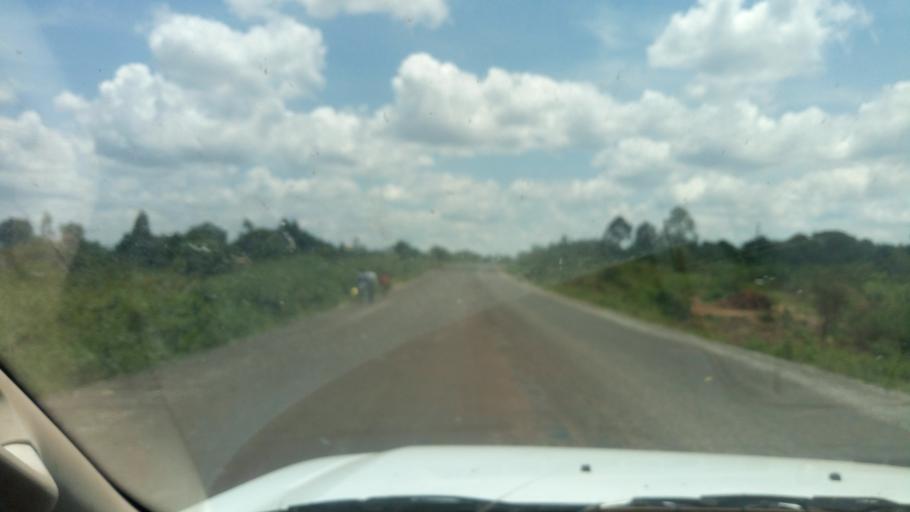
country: UG
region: Western Region
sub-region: Kiryandongo District
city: Kiryandongo
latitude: 1.7903
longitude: 31.9410
